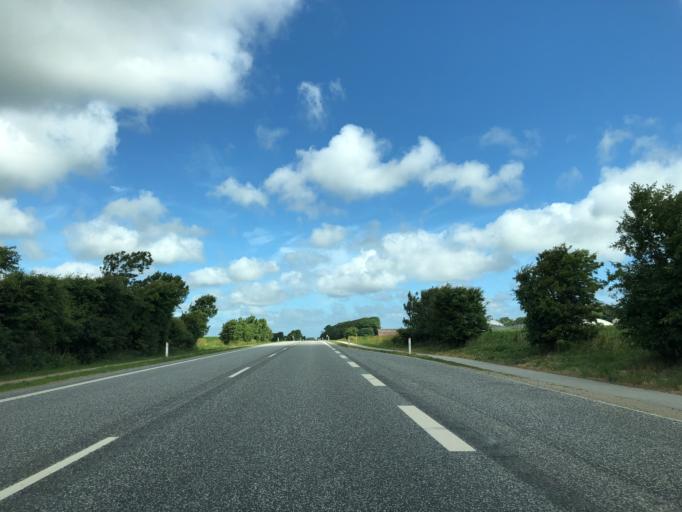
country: DK
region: Central Jutland
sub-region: Holstebro Kommune
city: Holstebro
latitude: 56.4230
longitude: 8.6004
